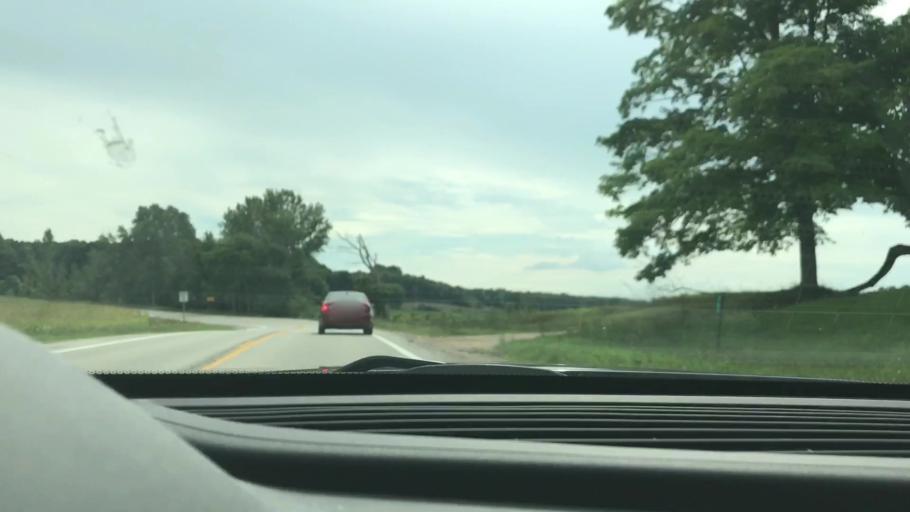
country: US
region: Michigan
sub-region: Antrim County
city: Bellaire
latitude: 45.0871
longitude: -85.2899
